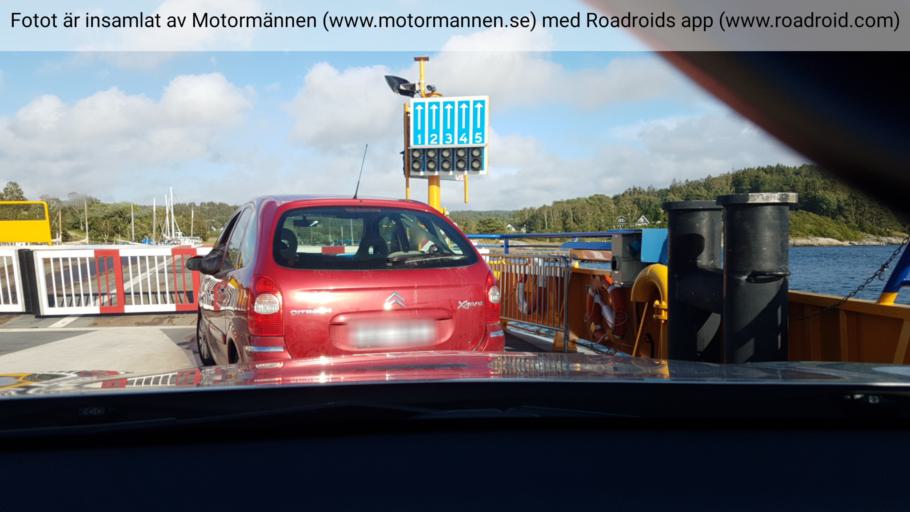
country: SE
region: Vaestra Goetaland
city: Svanesund
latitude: 58.1350
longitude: 11.8410
